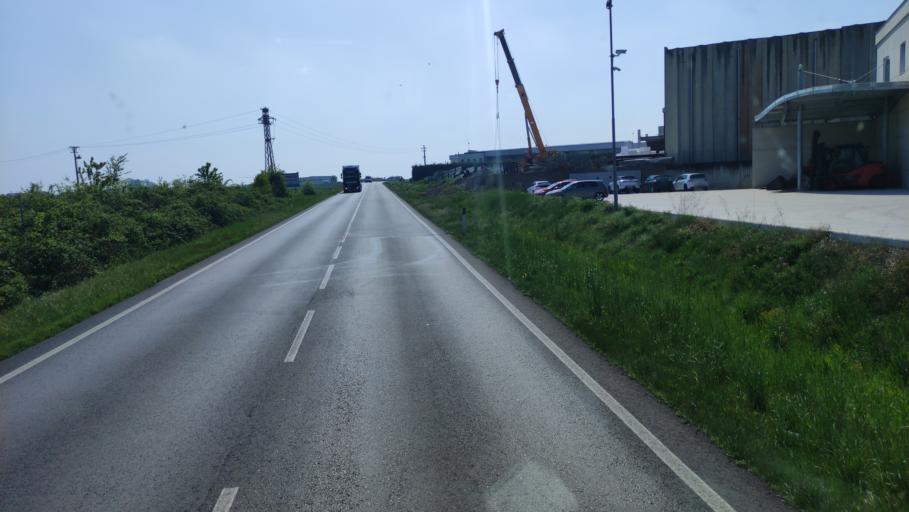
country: IT
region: Piedmont
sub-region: Provincia di Cuneo
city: Marene
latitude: 44.6615
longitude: 7.7473
